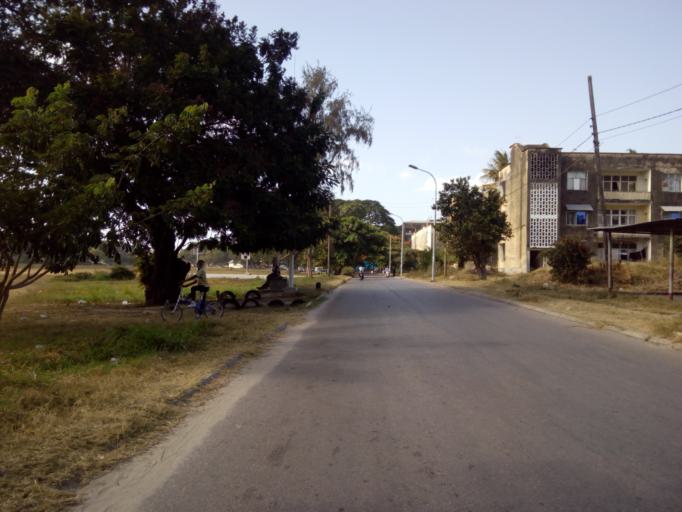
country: TZ
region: Zanzibar Urban/West
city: Zanzibar
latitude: -6.1713
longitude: 39.1945
